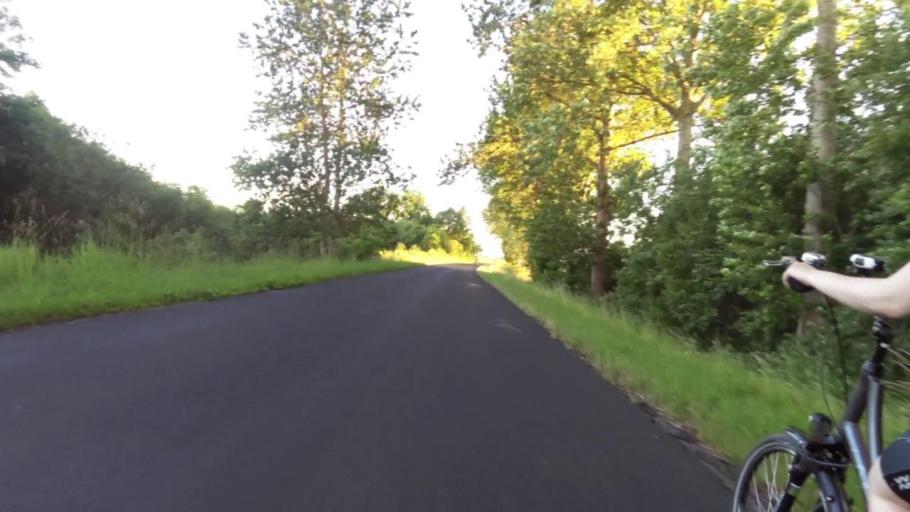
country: PL
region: West Pomeranian Voivodeship
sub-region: Powiat bialogardzki
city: Bialogard
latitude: 54.0327
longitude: 16.0413
